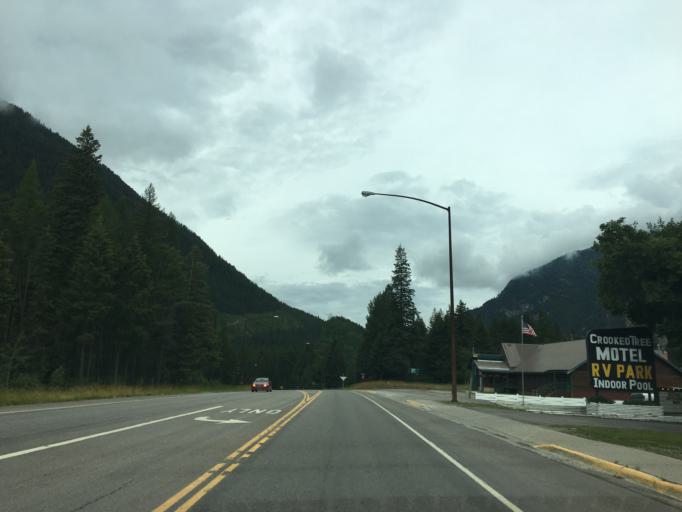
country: US
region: Montana
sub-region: Flathead County
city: Columbia Falls
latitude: 48.3857
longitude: -114.0716
